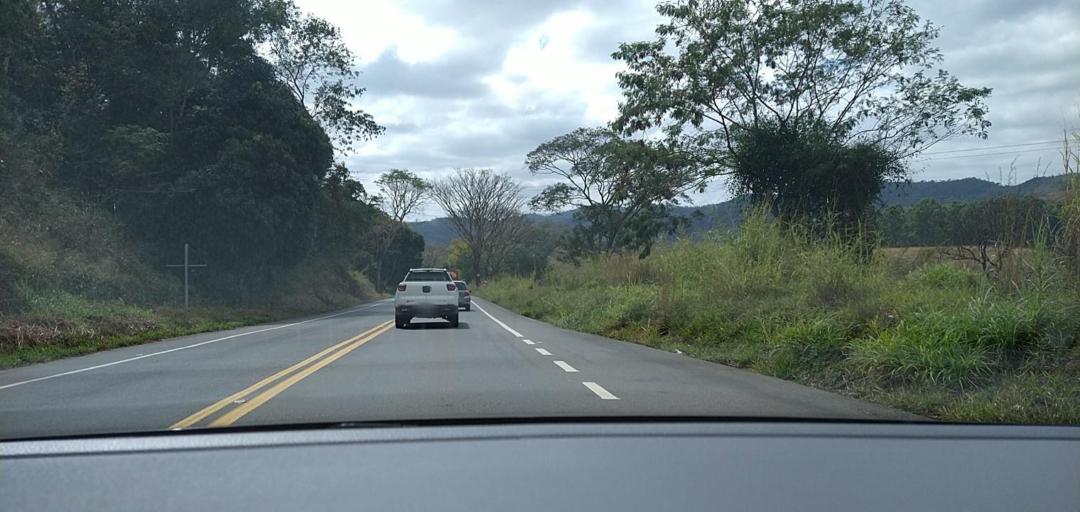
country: BR
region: Minas Gerais
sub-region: Ponte Nova
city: Ponte Nova
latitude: -20.5091
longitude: -42.8823
